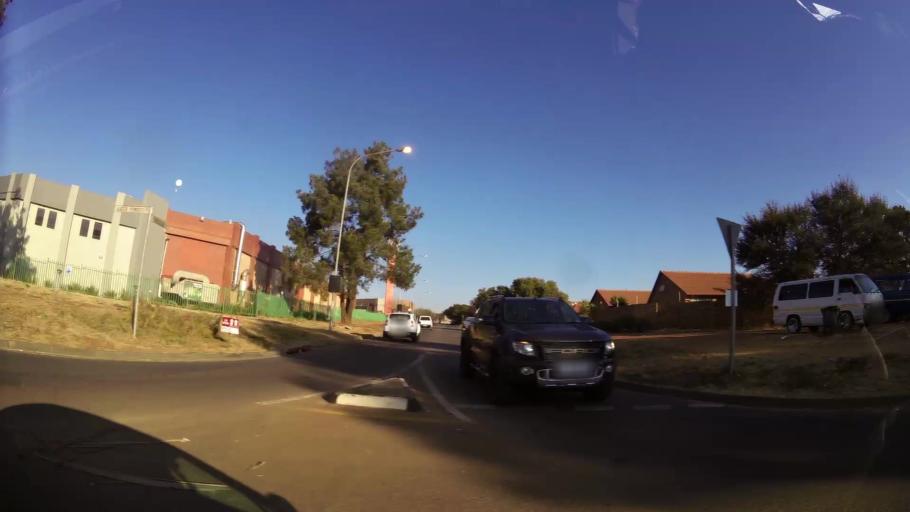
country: ZA
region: Gauteng
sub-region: City of Tshwane Metropolitan Municipality
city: Centurion
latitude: -25.8708
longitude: 28.1350
